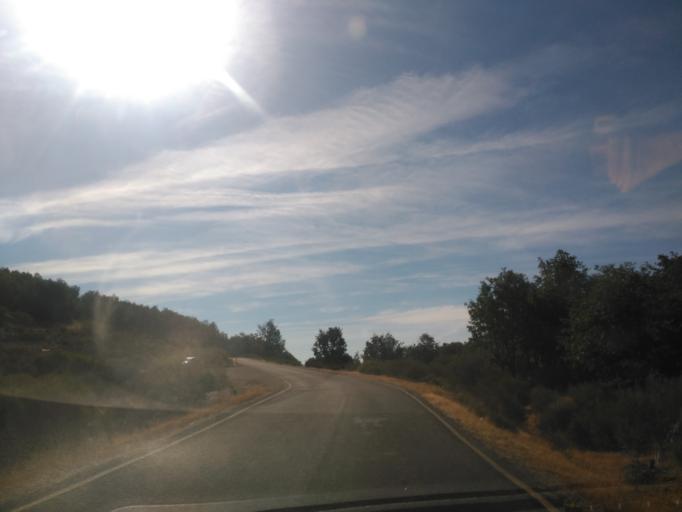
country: ES
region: Castille and Leon
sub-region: Provincia de Zamora
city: Cobreros
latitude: 42.1347
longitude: -6.7342
